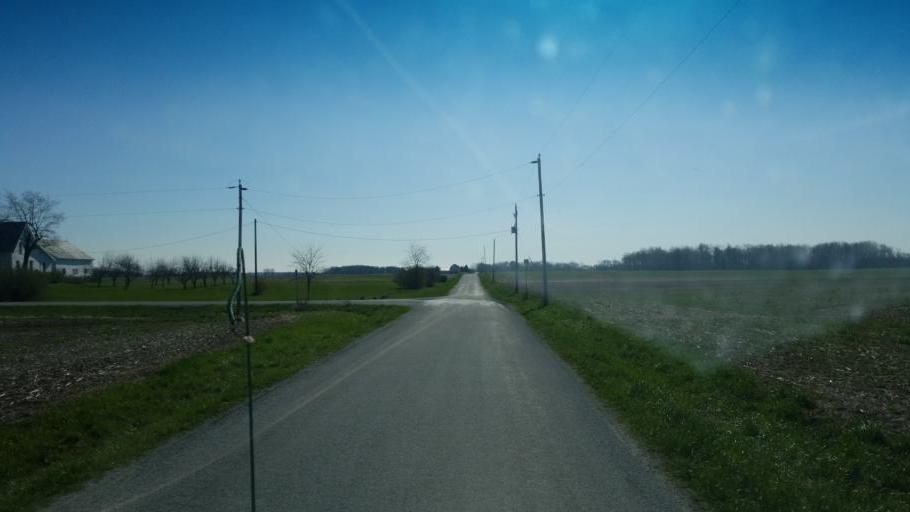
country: US
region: Ohio
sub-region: Hardin County
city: Kenton
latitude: 40.6806
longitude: -83.5599
